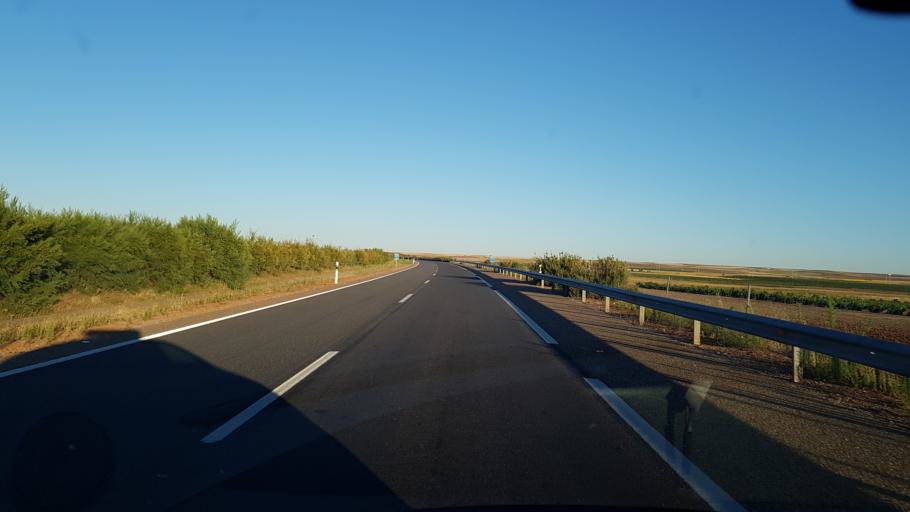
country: ES
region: Castille and Leon
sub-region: Provincia de Zamora
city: Morales de Toro
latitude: 41.5452
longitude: -5.3056
